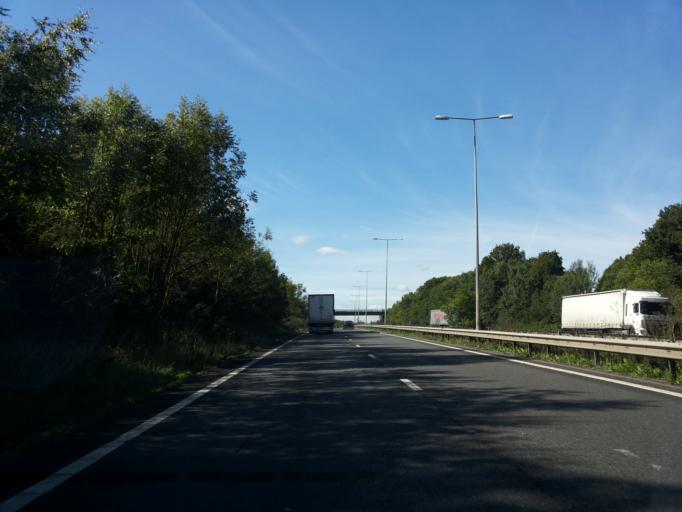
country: GB
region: England
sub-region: Kent
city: Dunkirk
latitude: 51.2895
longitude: 0.9850
